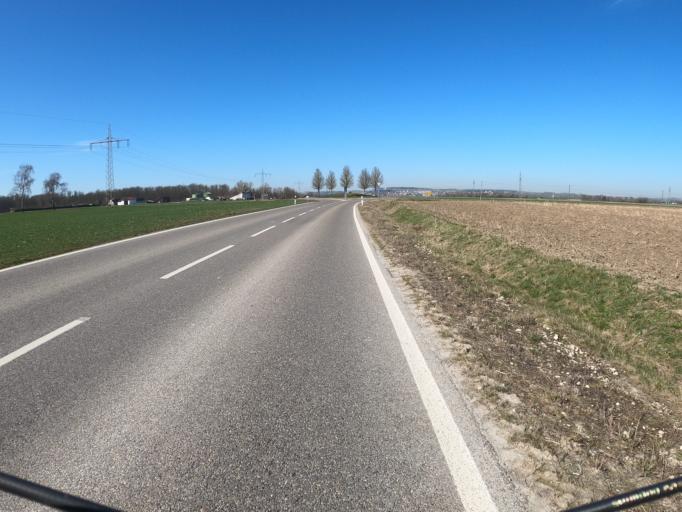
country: DE
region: Bavaria
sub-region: Swabia
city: Nersingen
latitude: 48.4536
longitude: 10.1511
